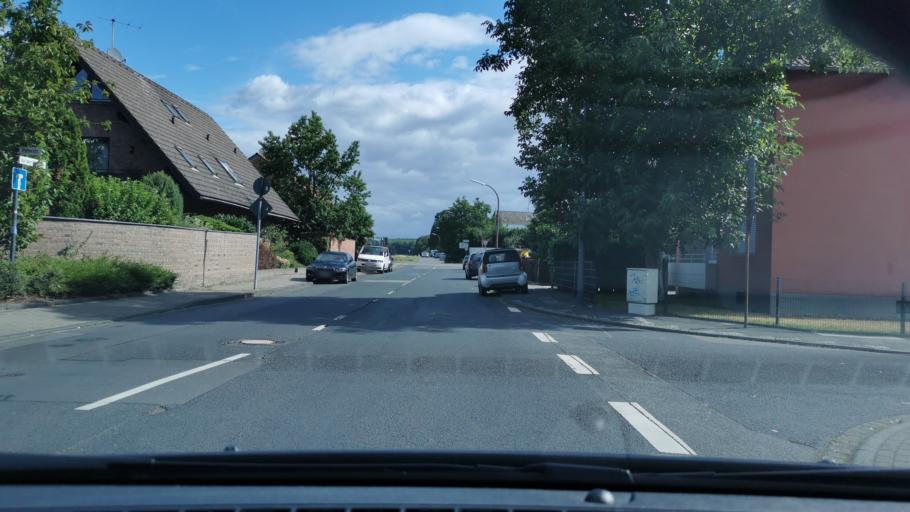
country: DE
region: North Rhine-Westphalia
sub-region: Regierungsbezirk Koln
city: Porz am Rhein
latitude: 50.8777
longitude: 7.0240
